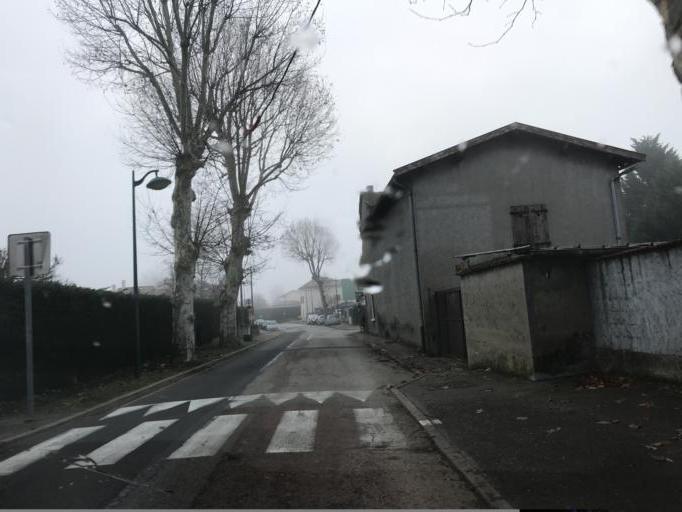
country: FR
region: Rhone-Alpes
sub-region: Departement de l'Ain
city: Mionnay
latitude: 45.8713
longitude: 4.9141
